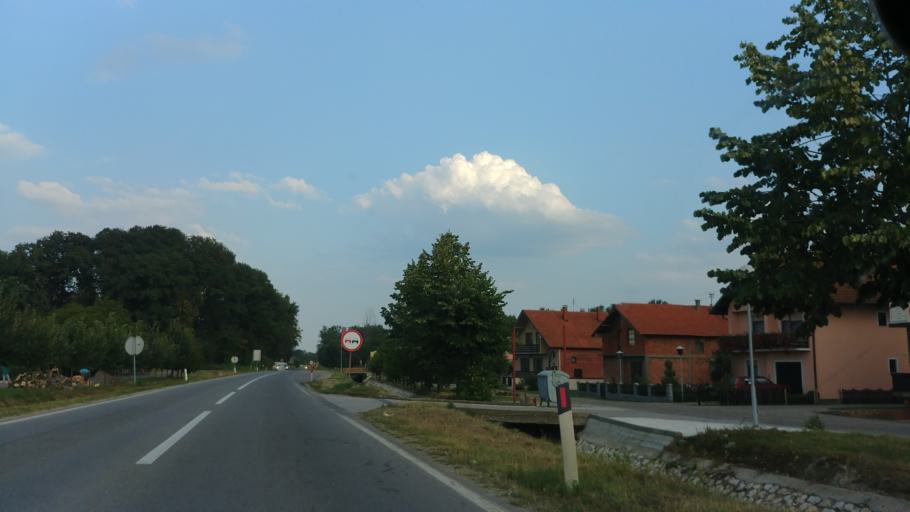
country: BA
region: Republika Srpska
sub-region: Opstina Ugljevik
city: Ugljevik
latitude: 44.6963
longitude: 19.0120
